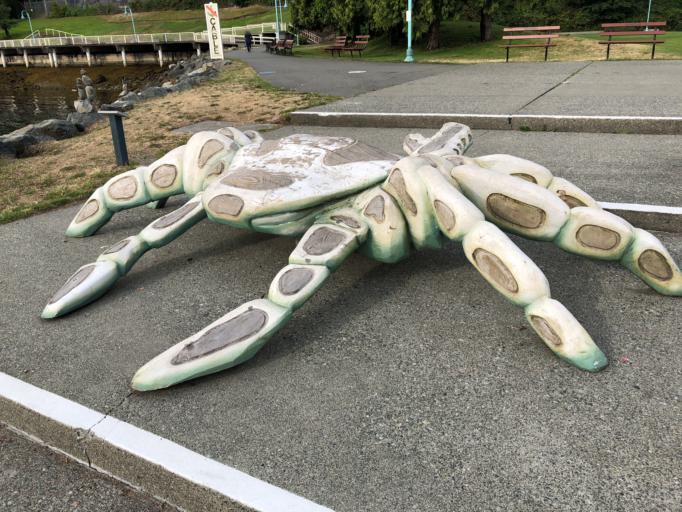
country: CA
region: British Columbia
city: Nanaimo
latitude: 49.1707
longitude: -123.9364
